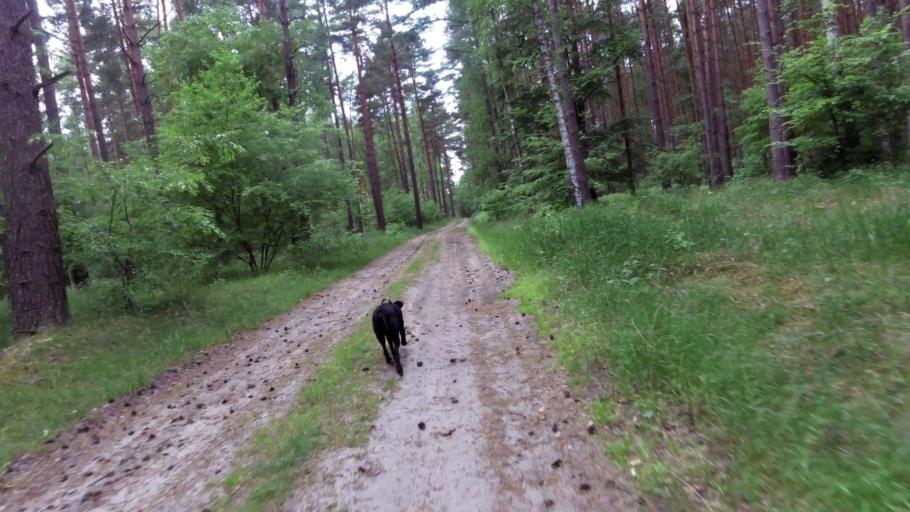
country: PL
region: West Pomeranian Voivodeship
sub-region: Powiat mysliborski
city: Debno
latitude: 52.8144
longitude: 14.6605
